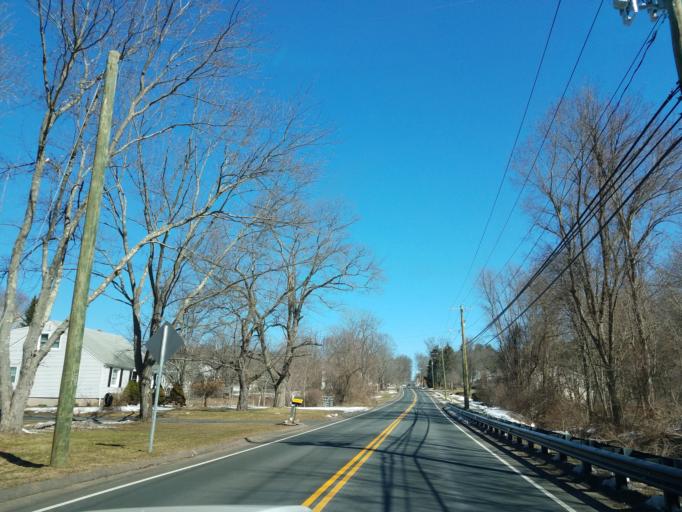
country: US
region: Connecticut
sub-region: Hartford County
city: Manchester
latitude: 41.8289
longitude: -72.5171
